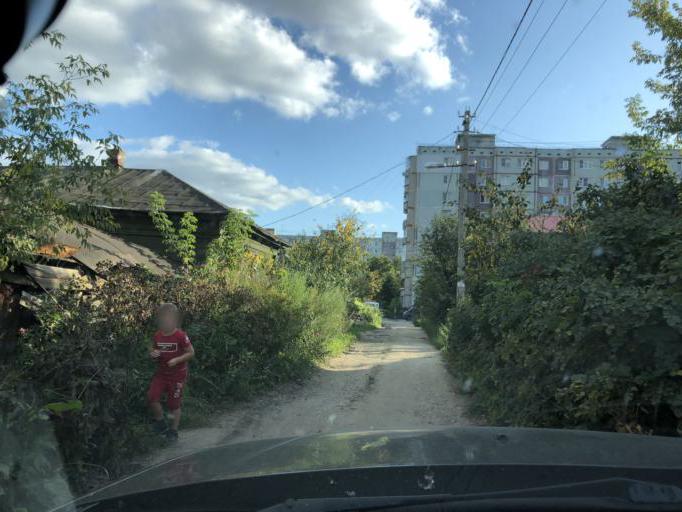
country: RU
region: Tula
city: Tula
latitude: 54.2114
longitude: 37.6063
